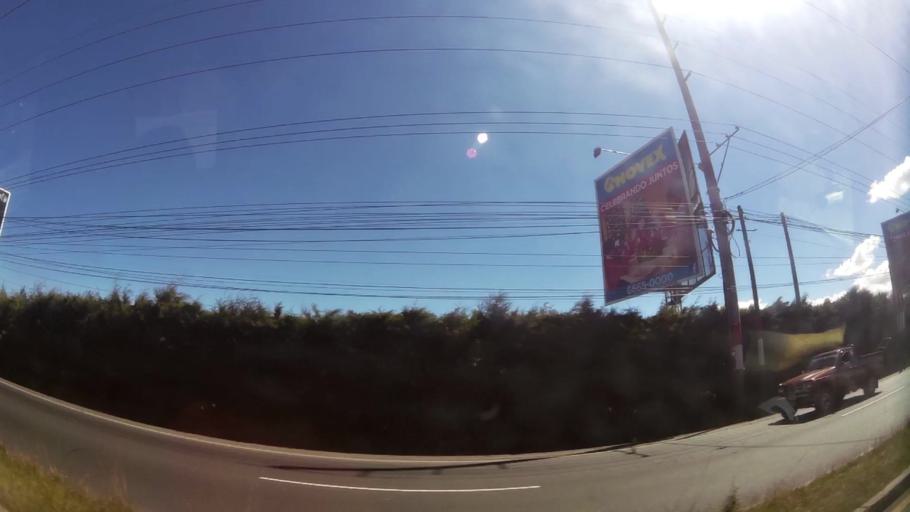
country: GT
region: Guatemala
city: Santa Catarina Pinula
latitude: 14.5162
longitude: -90.4738
